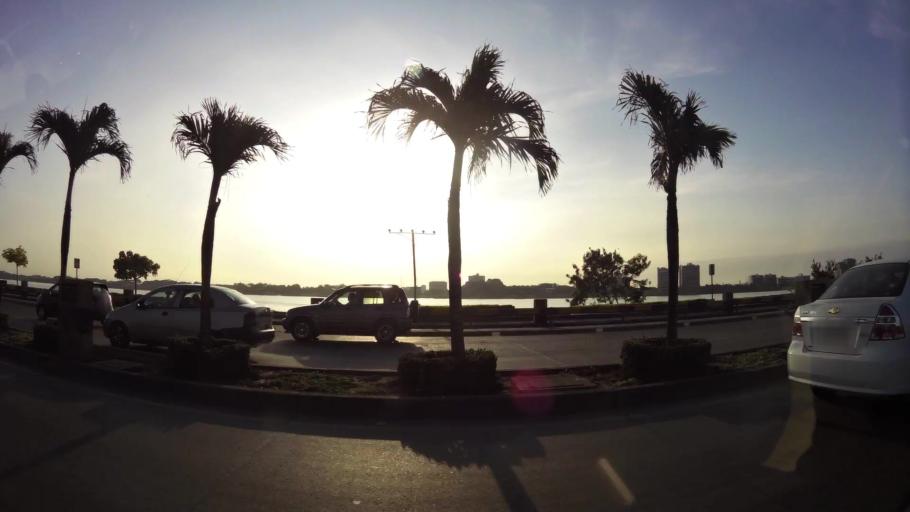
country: EC
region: Guayas
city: Eloy Alfaro
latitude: -2.1455
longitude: -79.8769
